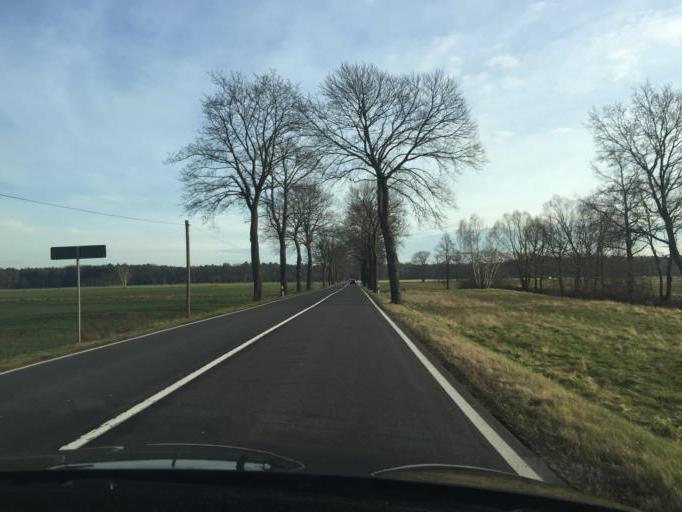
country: DE
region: Brandenburg
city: Cottbus
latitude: 51.7357
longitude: 14.4124
